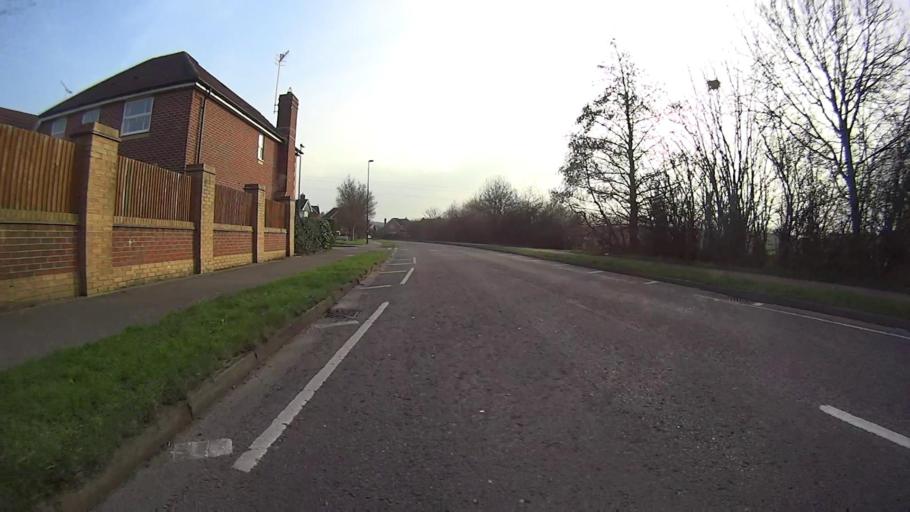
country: GB
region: England
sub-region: West Sussex
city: Maidenbower
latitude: 51.1046
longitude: -0.1493
